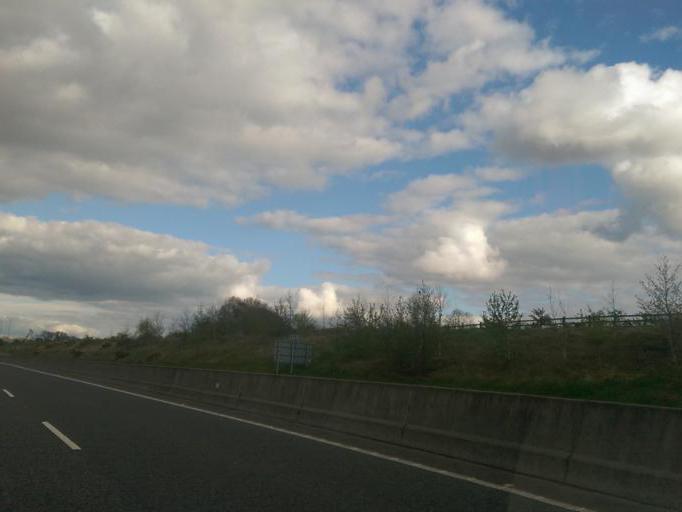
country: IE
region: Leinster
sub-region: An Iarmhi
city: Moate
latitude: 53.3944
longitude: -7.7980
